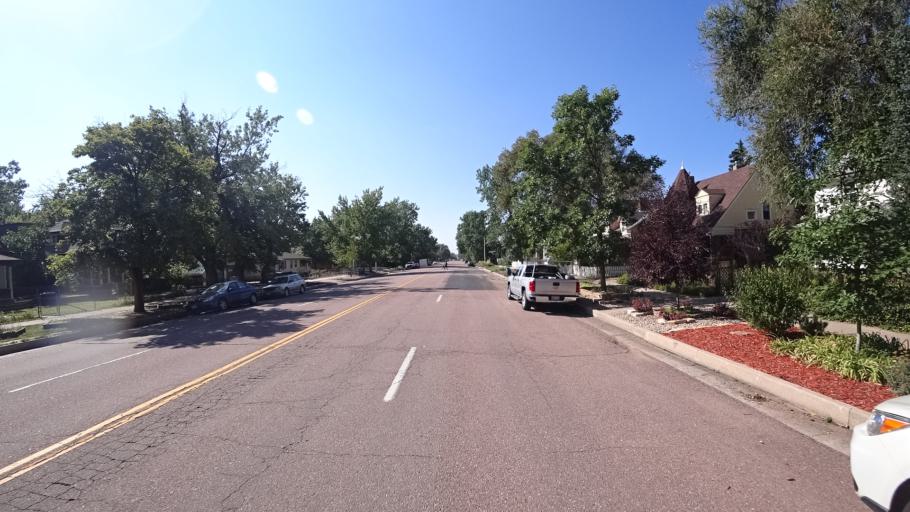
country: US
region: Colorado
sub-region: El Paso County
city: Colorado Springs
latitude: 38.8544
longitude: -104.8188
